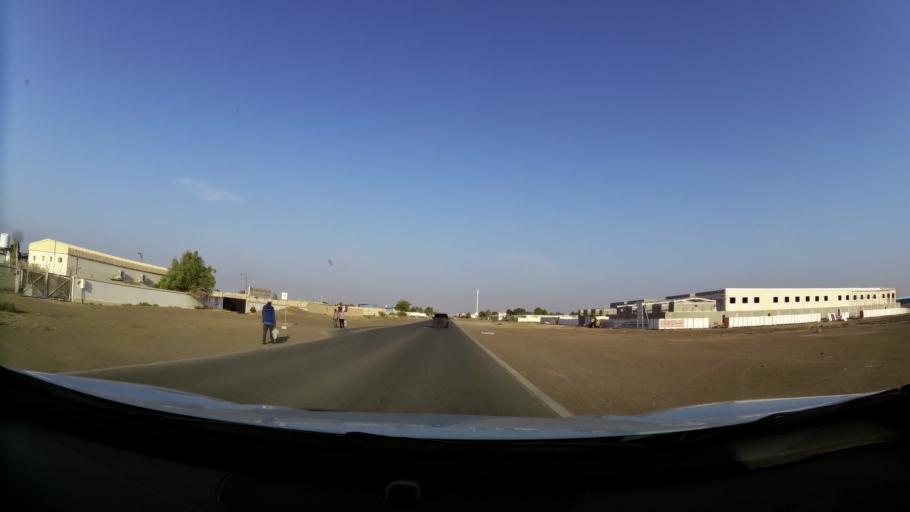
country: AE
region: Abu Dhabi
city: Al Ain
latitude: 24.1407
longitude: 55.8283
